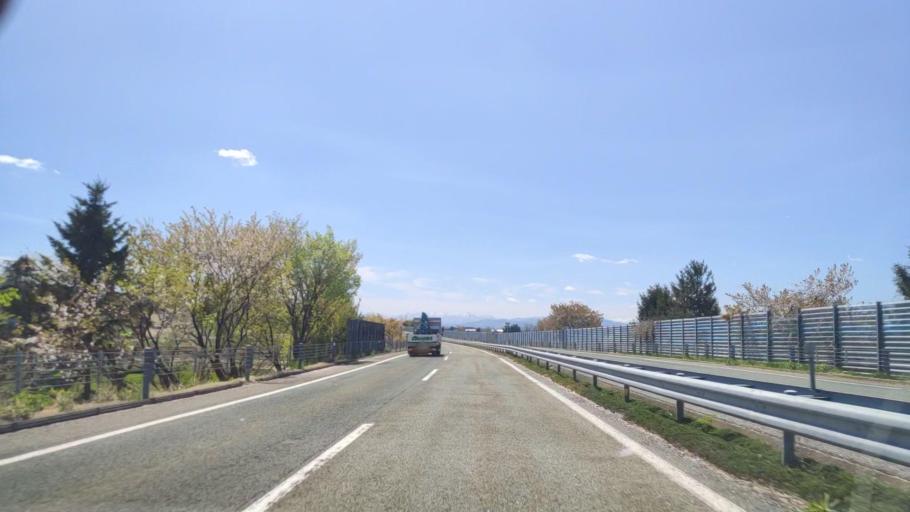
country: JP
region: Akita
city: Yokotemachi
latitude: 39.3132
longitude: 140.5159
